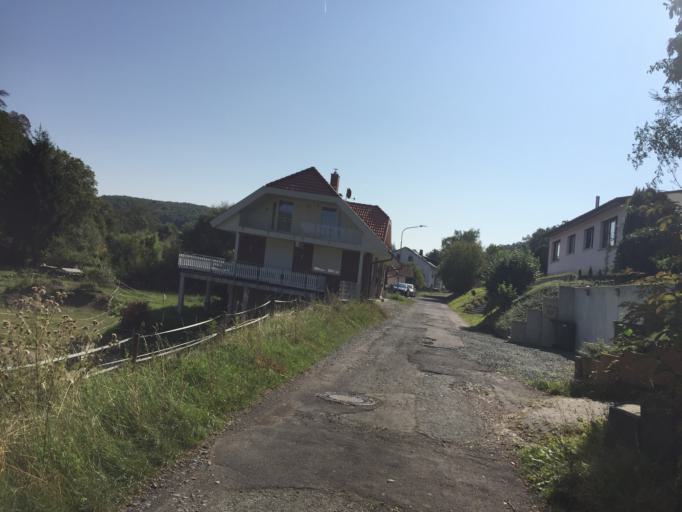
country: DE
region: Hesse
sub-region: Regierungsbezirk Giessen
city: Schoeffengrund
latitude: 50.4466
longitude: 8.5650
